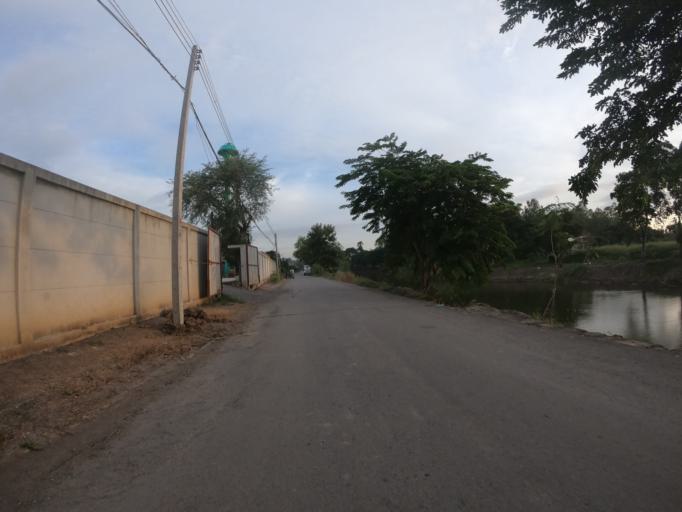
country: TH
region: Pathum Thani
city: Ban Lam Luk Ka
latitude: 14.0064
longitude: 100.7986
